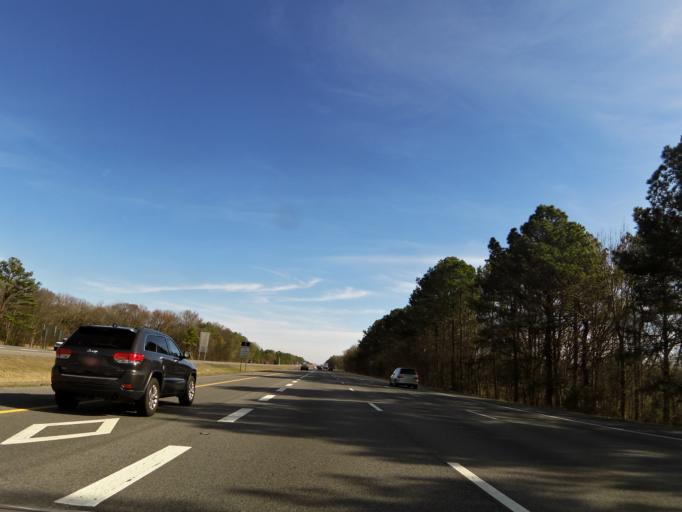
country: US
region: Tennessee
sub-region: Rutherford County
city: Smyrna
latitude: 35.9127
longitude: -86.5076
